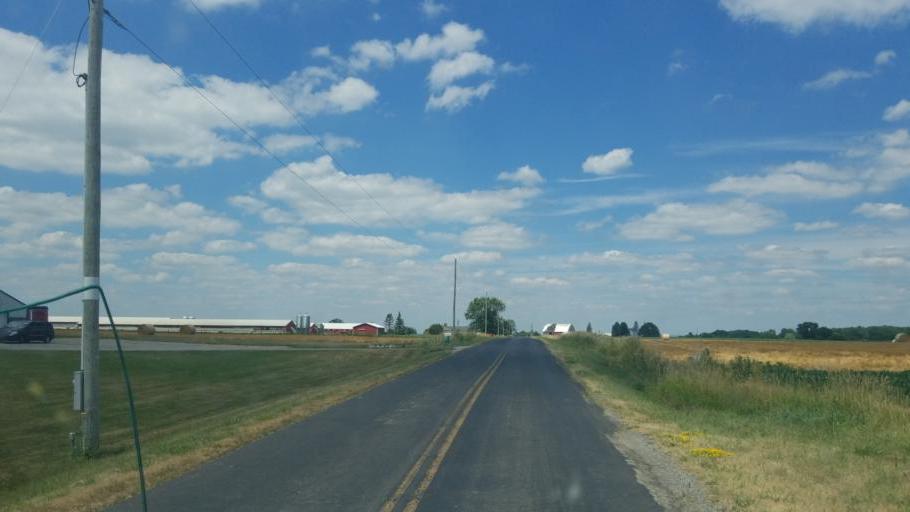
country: US
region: Ohio
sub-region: Williams County
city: Edgerton
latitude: 41.4580
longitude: -84.7104
